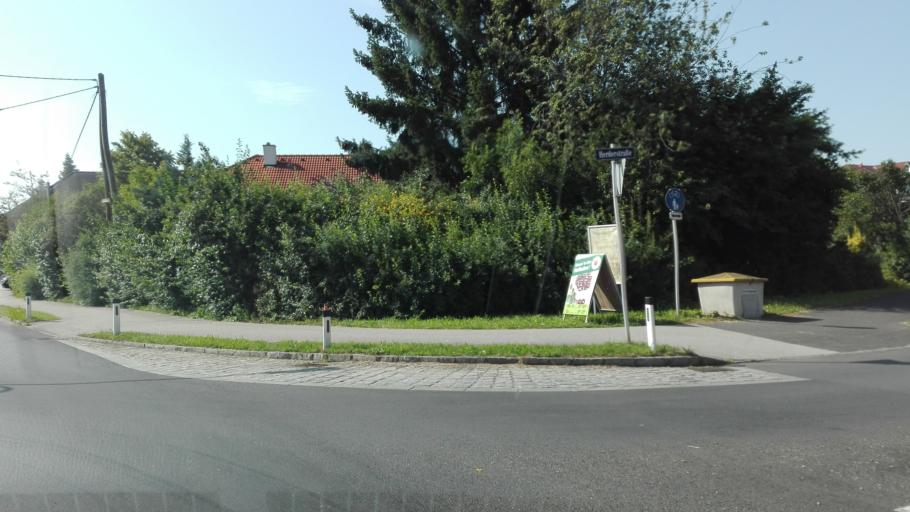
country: AT
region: Upper Austria
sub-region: Politischer Bezirk Linz-Land
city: Leonding
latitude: 48.2637
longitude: 14.2634
